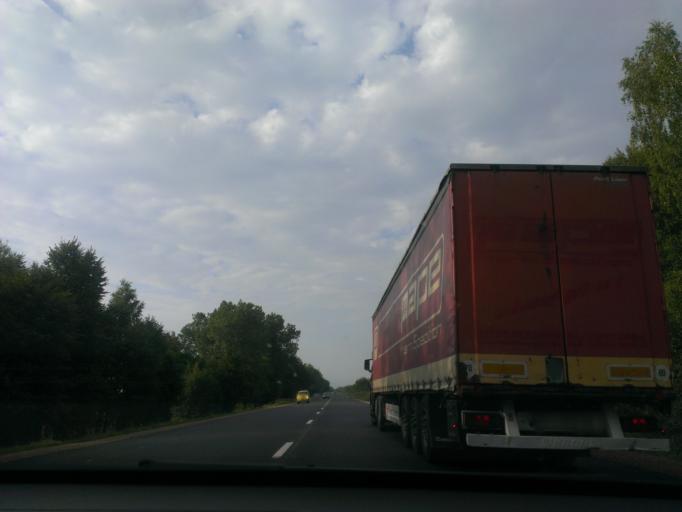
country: LV
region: Lecava
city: Iecava
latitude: 56.6706
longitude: 24.2352
